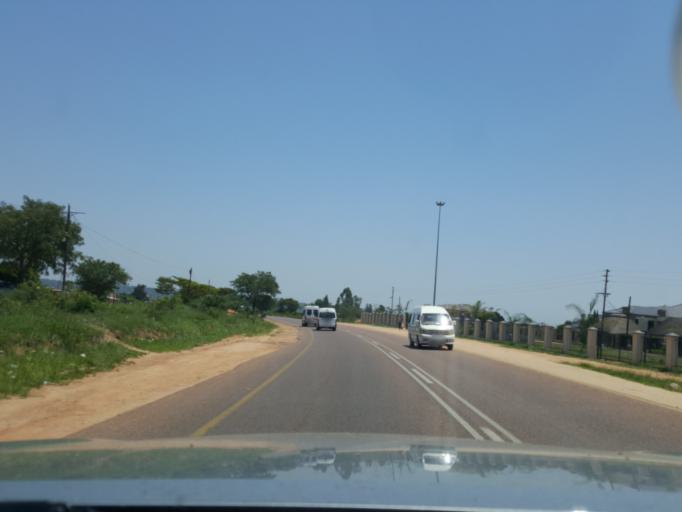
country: ZA
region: Limpopo
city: Thulamahashi
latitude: -24.7640
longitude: 31.0435
